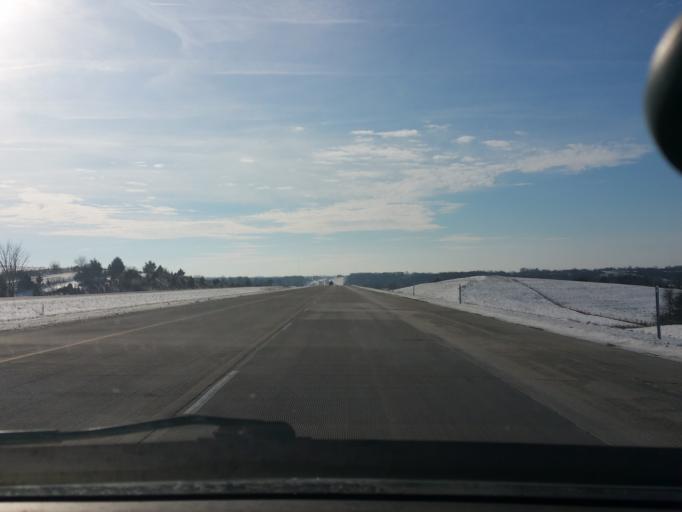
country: US
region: Iowa
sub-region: Warren County
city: Norwalk
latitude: 41.4762
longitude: -93.7805
